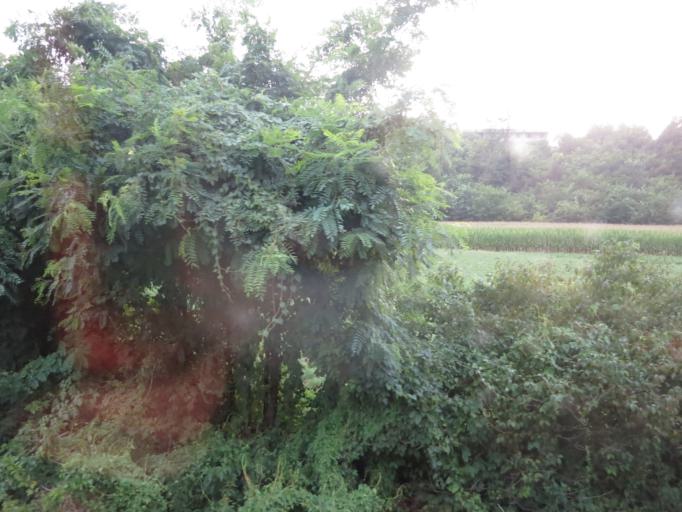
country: IT
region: Lombardy
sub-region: Provincia di Monza e Brianza
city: Lentate sul Seveso
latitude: 45.6849
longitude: 9.1241
